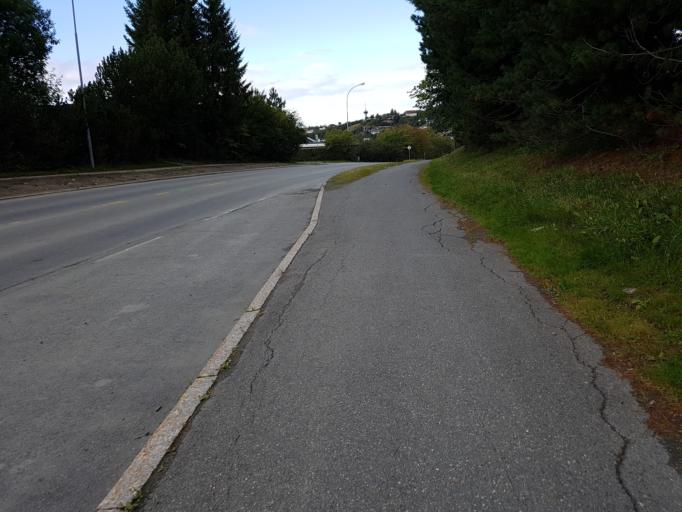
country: NO
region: Sor-Trondelag
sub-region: Trondheim
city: Trondheim
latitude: 63.4008
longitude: 10.4230
